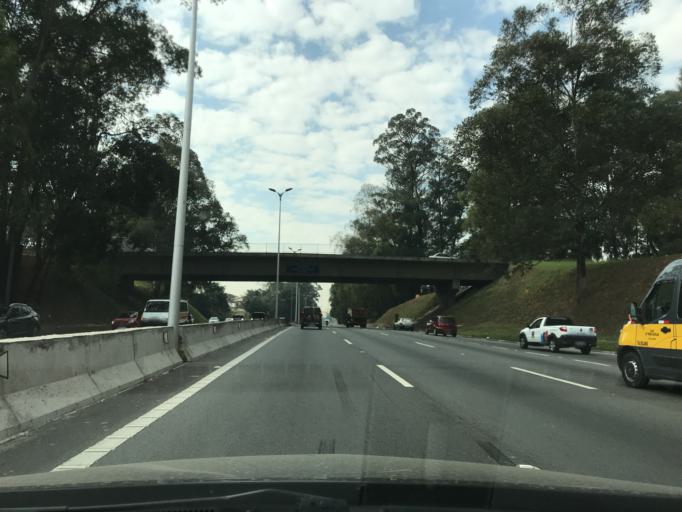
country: BR
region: Sao Paulo
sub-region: Taboao Da Serra
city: Taboao da Serra
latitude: -23.5855
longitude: -46.7637
